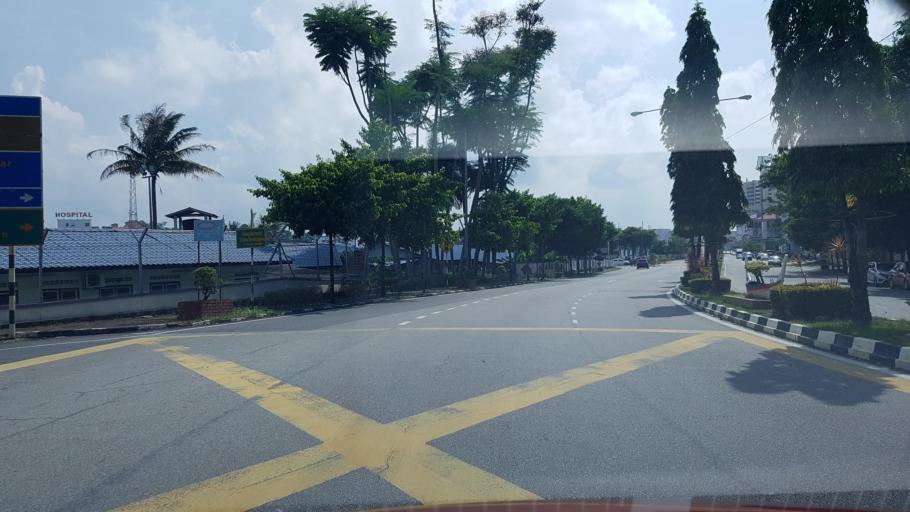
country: MY
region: Terengganu
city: Kuala Terengganu
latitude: 5.3278
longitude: 103.1425
